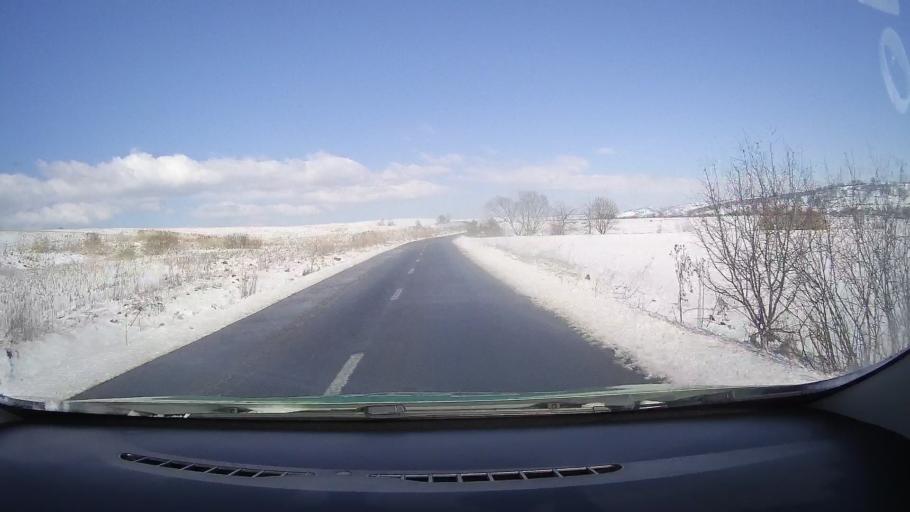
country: RO
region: Sibiu
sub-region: Comuna Rosia
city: Rosia
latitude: 45.8438
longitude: 24.3055
